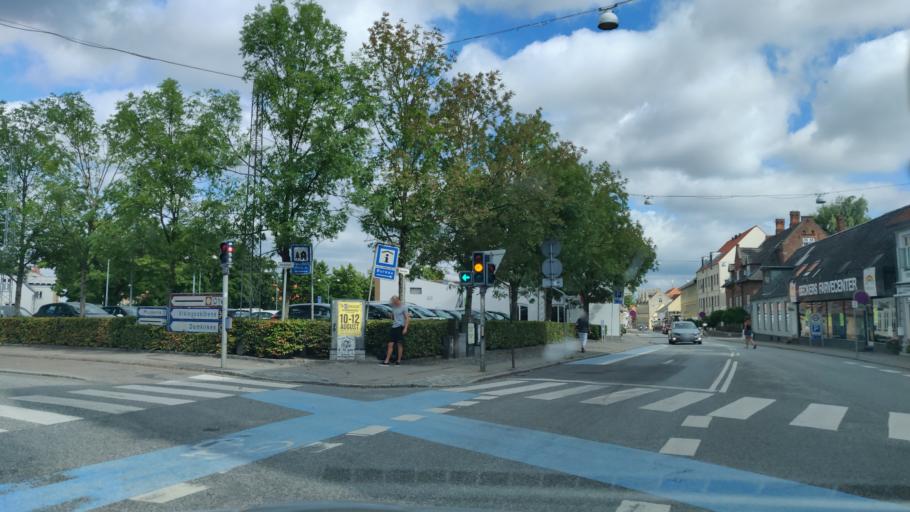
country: DK
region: Zealand
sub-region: Roskilde Kommune
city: Roskilde
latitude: 55.6380
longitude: 12.0762
